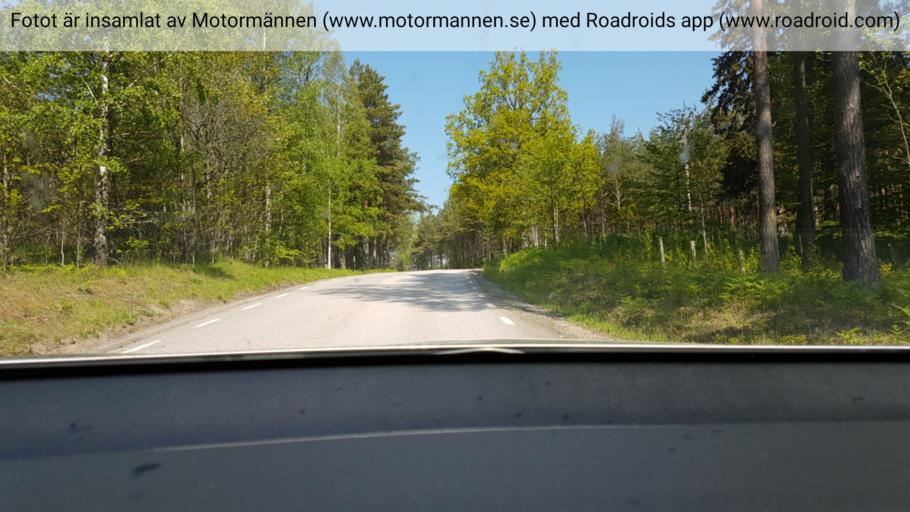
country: SE
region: Kalmar
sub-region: Vasterviks Kommun
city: Forserum
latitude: 57.8418
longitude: 16.5376
